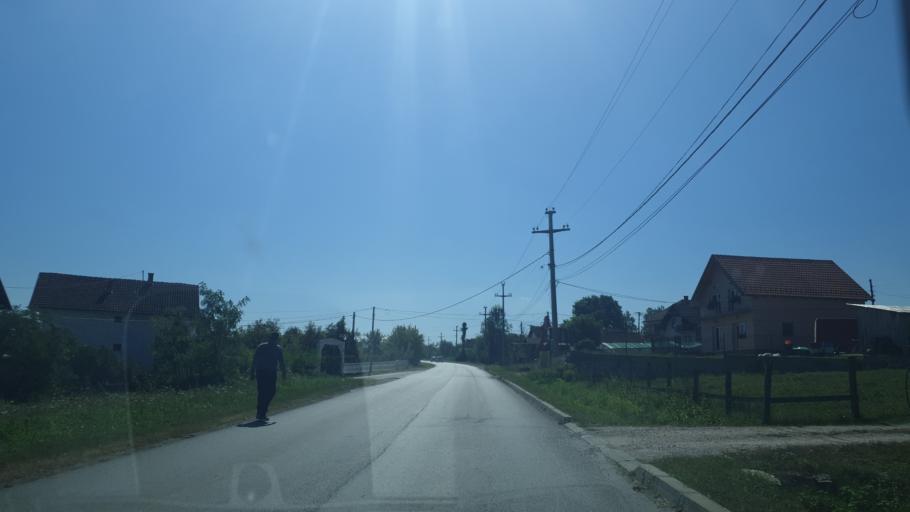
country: RS
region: Central Serbia
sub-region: Kolubarski Okrug
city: Mionica
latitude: 44.2479
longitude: 20.0788
